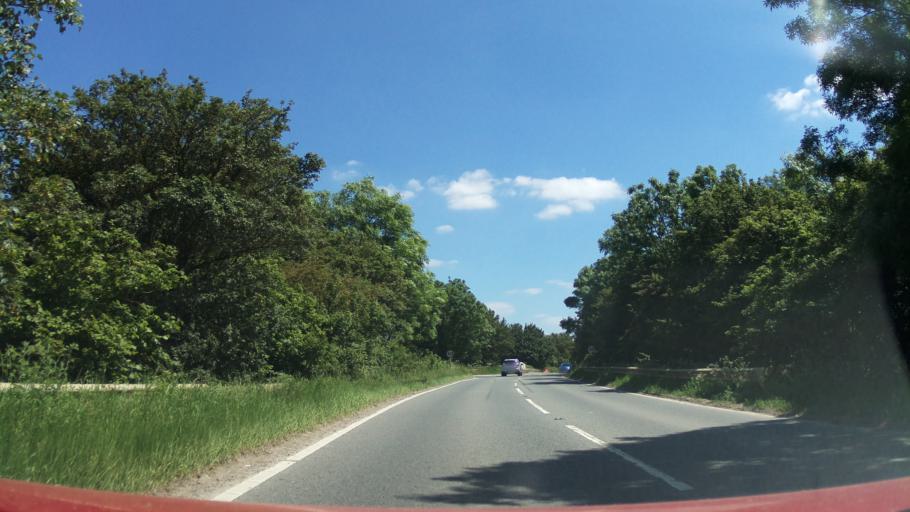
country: GB
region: England
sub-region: Wiltshire
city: Lydiard Tregoze
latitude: 51.5412
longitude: -1.8470
